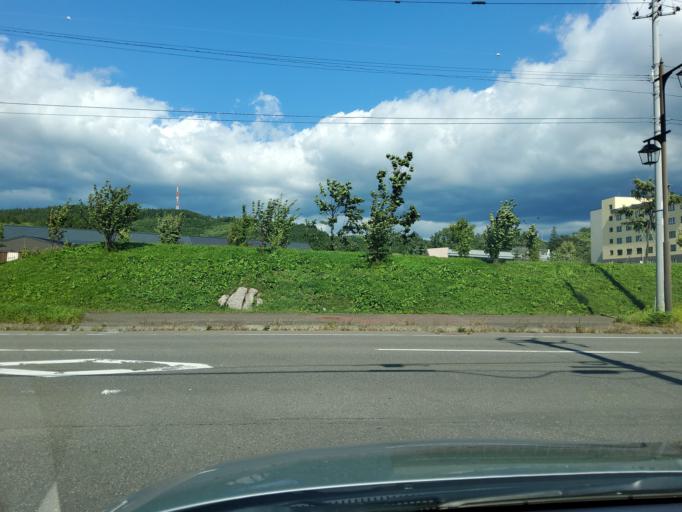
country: JP
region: Hokkaido
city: Obihiro
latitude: 42.9327
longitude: 143.3006
